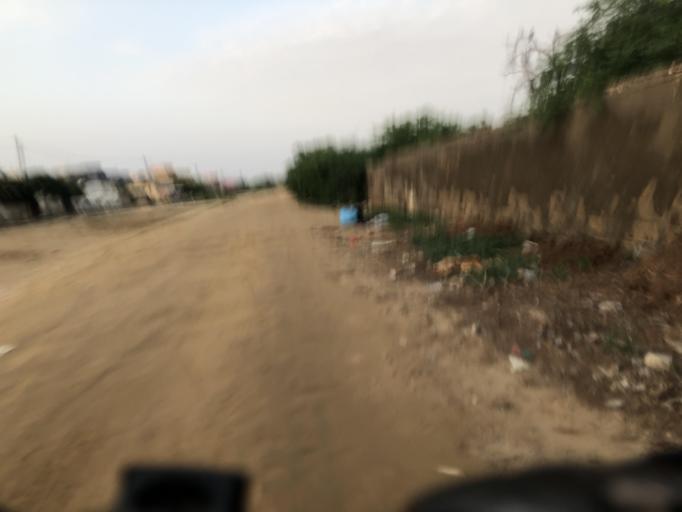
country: SN
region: Saint-Louis
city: Saint-Louis
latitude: 16.0521
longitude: -16.4329
